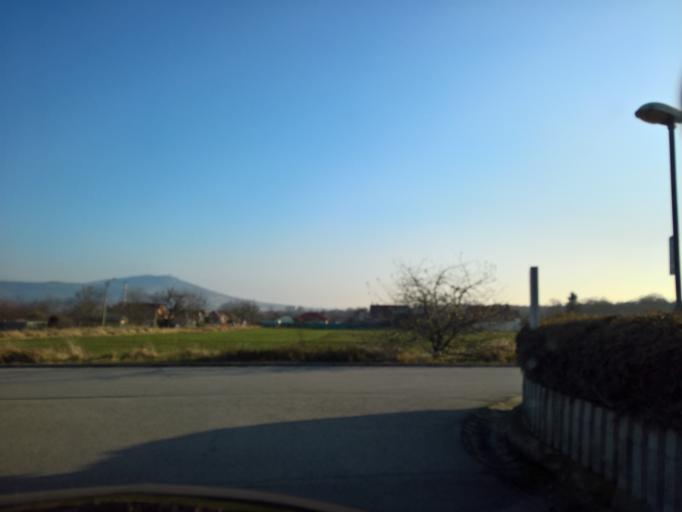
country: SK
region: Nitriansky
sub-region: Okres Nitra
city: Nitra
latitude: 48.3153
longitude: 18.0304
